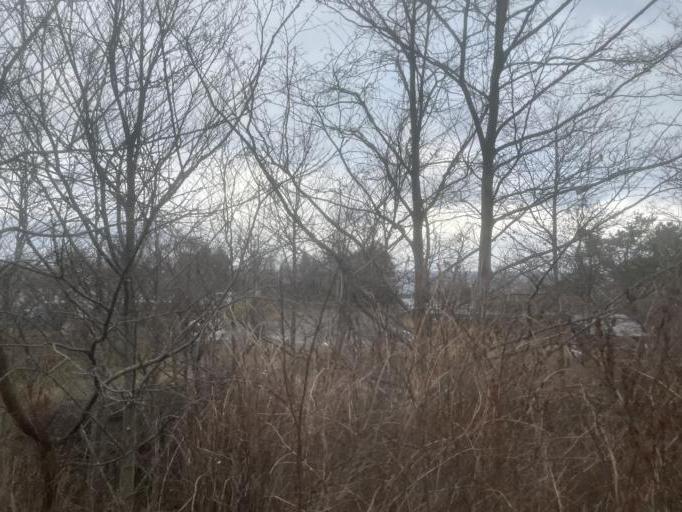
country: JP
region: Aomori
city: Shimokizukuri
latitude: 41.1807
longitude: 140.4701
